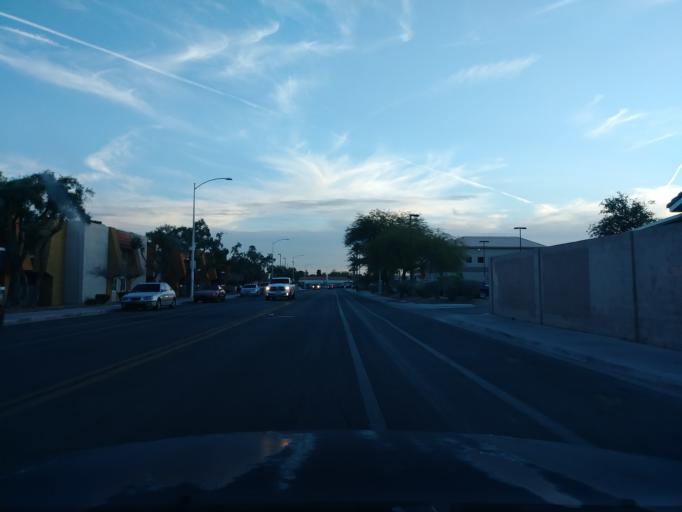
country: US
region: Nevada
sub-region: Clark County
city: Spring Valley
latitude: 36.1613
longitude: -115.2420
